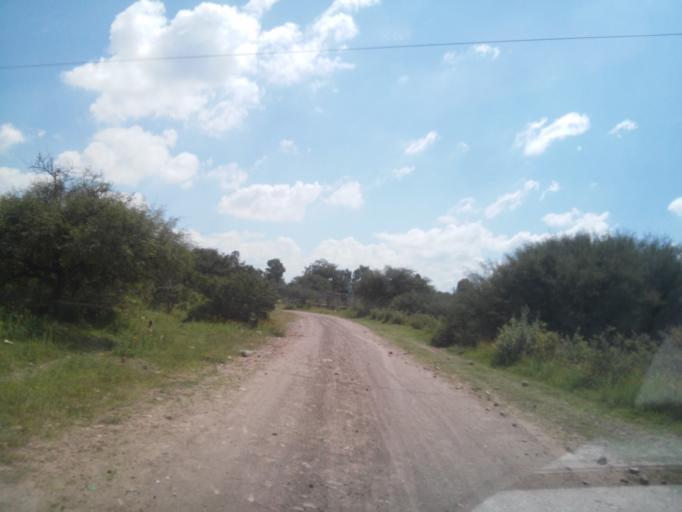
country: MX
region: Durango
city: Victoria de Durango
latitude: 24.0129
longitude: -104.7416
